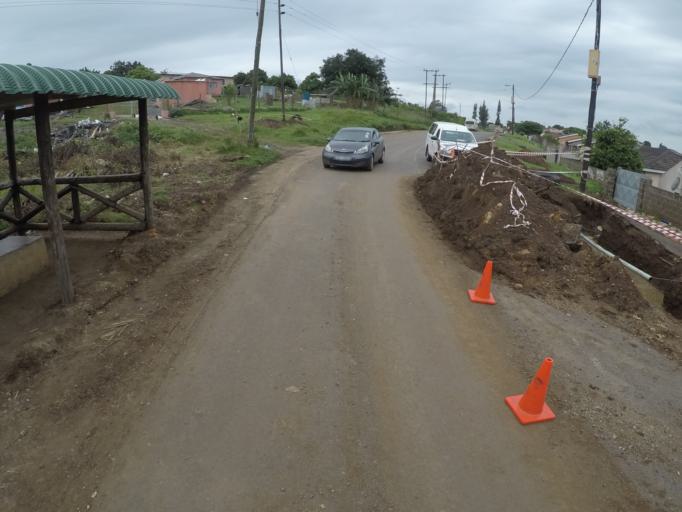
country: ZA
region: KwaZulu-Natal
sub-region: uThungulu District Municipality
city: Empangeni
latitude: -28.7726
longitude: 31.8509
